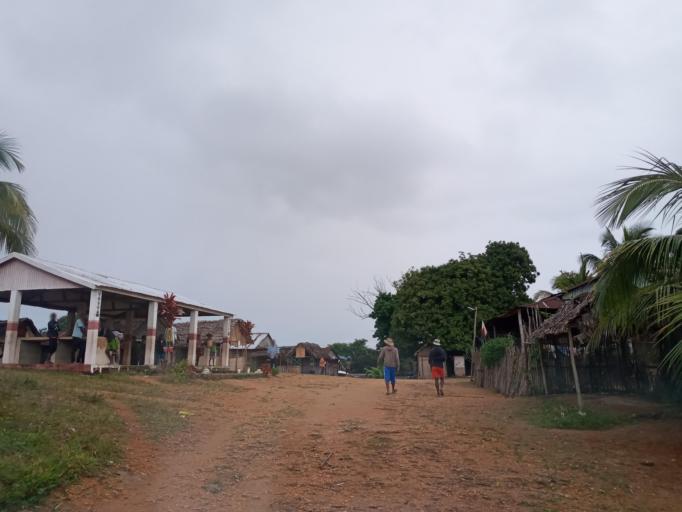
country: MG
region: Atsimo-Atsinanana
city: Vohipaho
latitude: -23.9733
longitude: 47.3336
